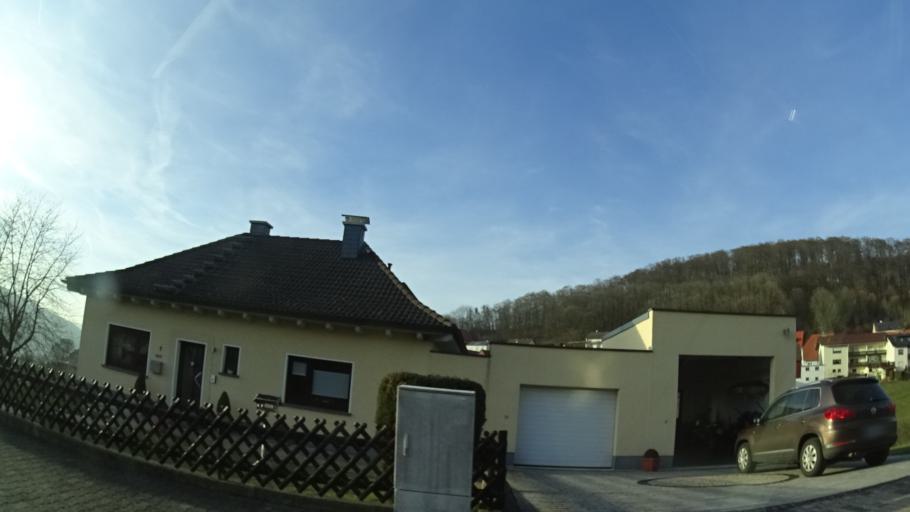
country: DE
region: Bavaria
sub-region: Regierungsbezirk Unterfranken
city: Zeitlofs
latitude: 50.2982
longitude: 9.6764
